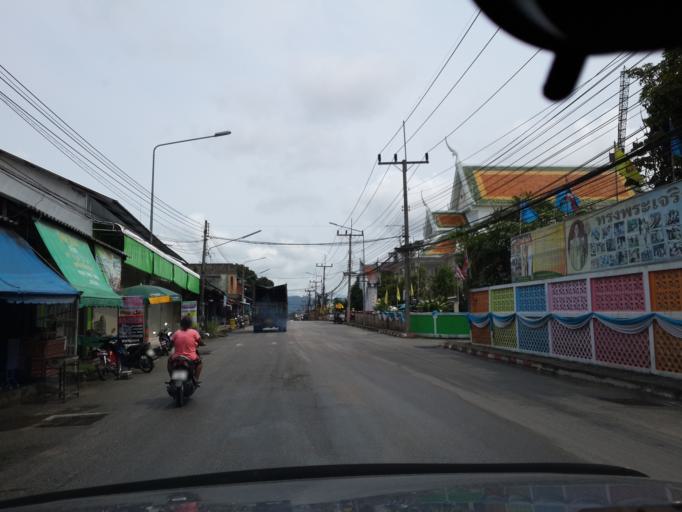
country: TH
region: Narathiwat
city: Rueso
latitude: 6.3874
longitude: 101.5139
